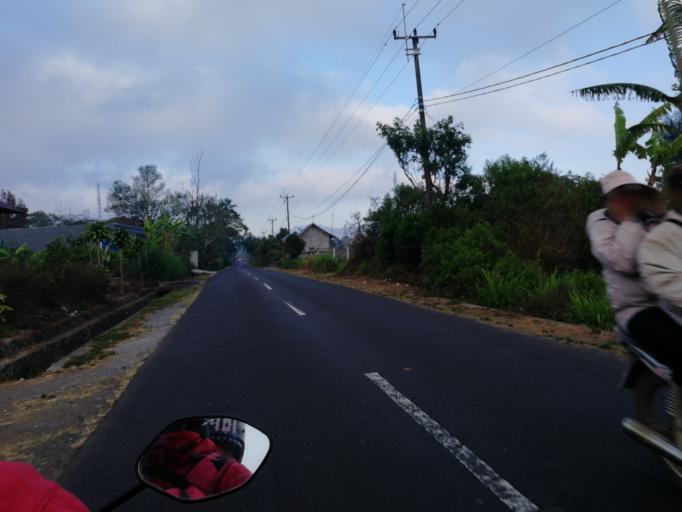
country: ID
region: Bali
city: Banjar Padangbulia
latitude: -8.2241
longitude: 115.2474
